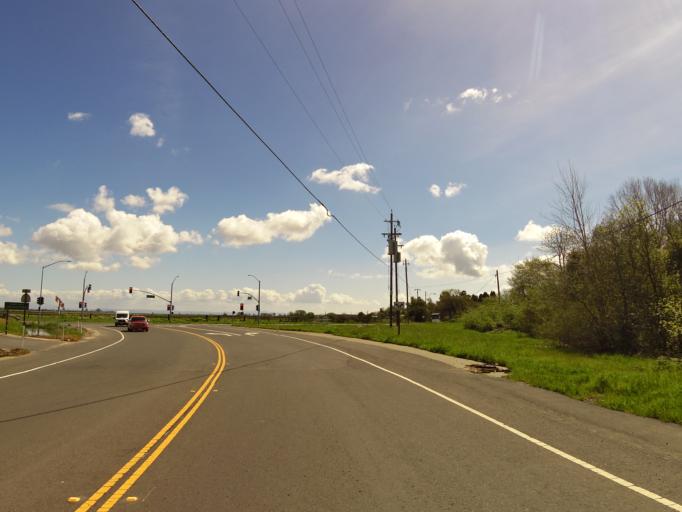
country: US
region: California
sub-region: Sonoma County
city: Sonoma
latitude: 38.2438
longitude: -122.4491
